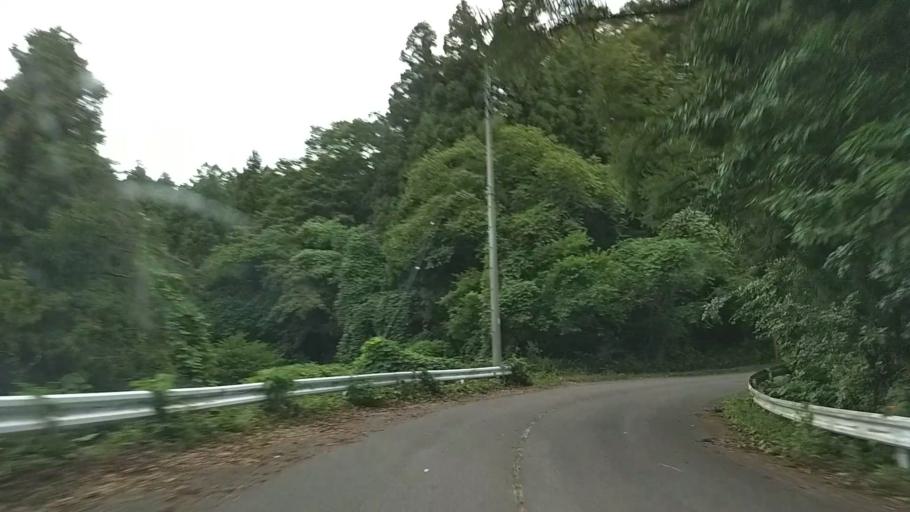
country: JP
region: Nagano
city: Iiyama
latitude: 36.8153
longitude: 138.3697
